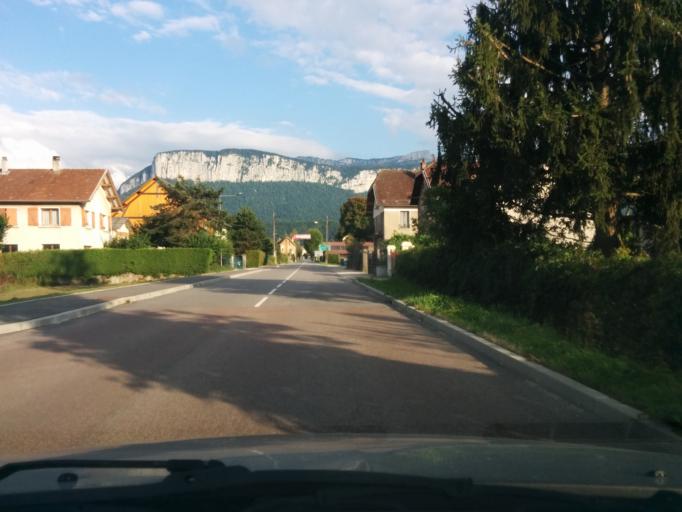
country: FR
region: Rhone-Alpes
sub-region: Departement de la Savoie
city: Les Echelles
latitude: 45.4412
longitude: 5.7468
